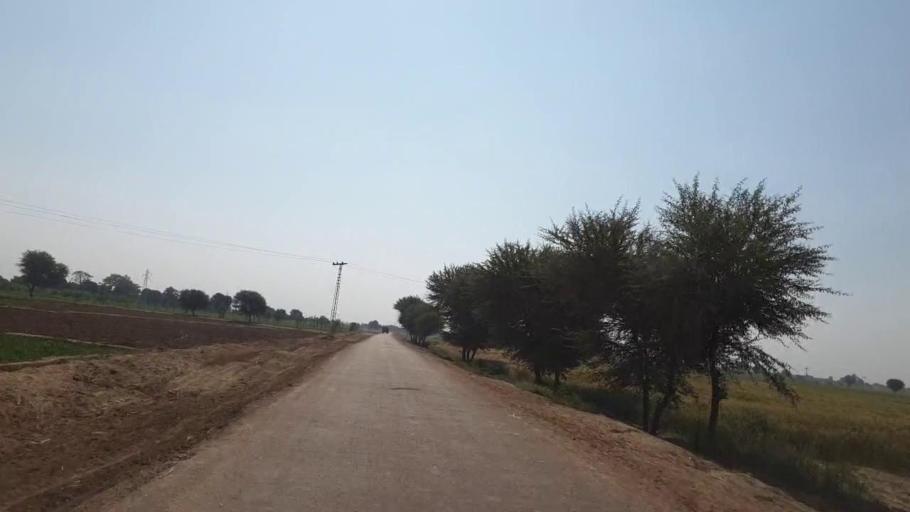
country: PK
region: Sindh
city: Kunri
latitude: 25.1643
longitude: 69.5474
